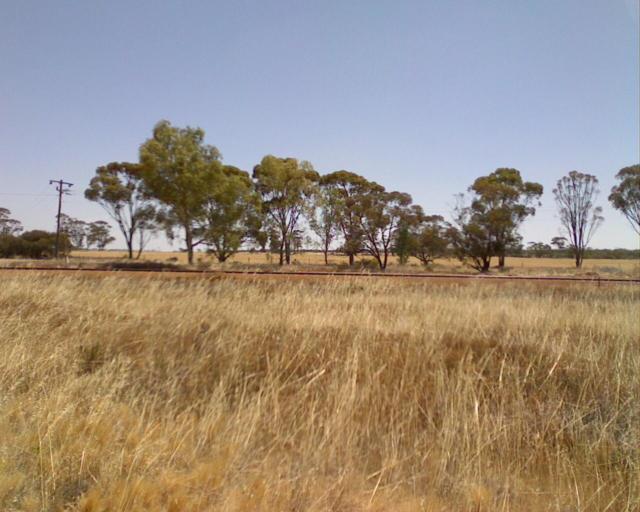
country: AU
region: Western Australia
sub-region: Wongan-Ballidu
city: Wongan Hills
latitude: -30.4543
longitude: 117.5256
